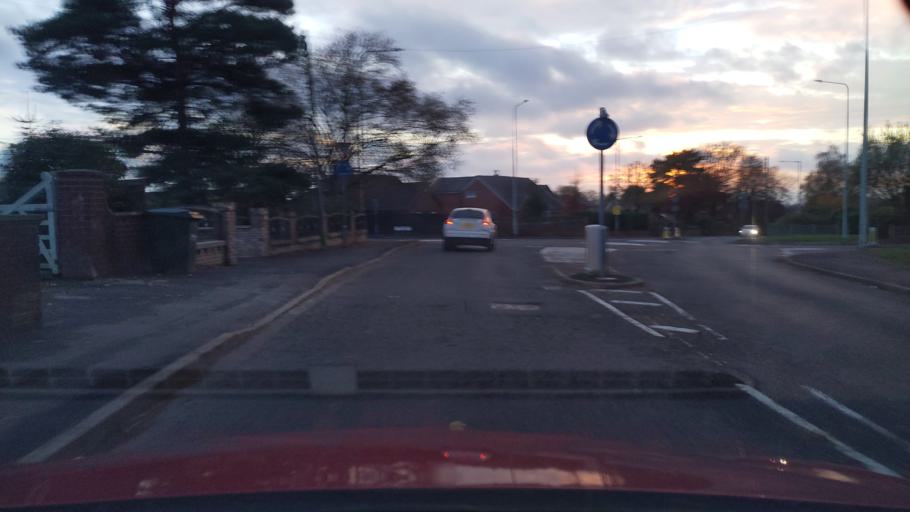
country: GB
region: England
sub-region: Lancashire
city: Clayton-le-Woods
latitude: 53.6983
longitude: -2.6608
